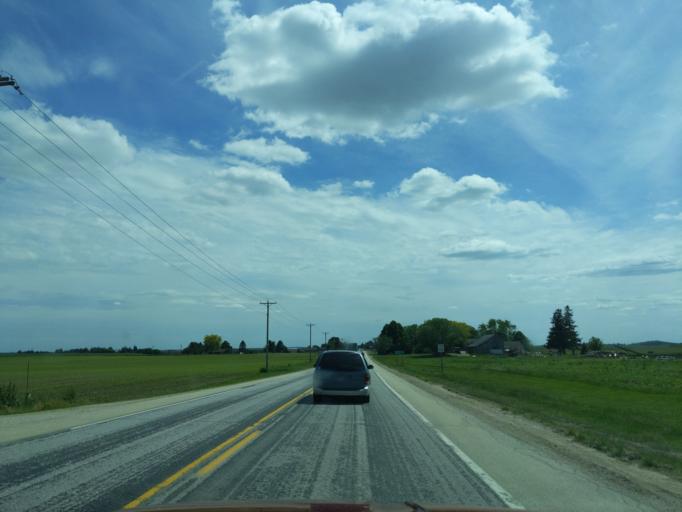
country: US
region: Wisconsin
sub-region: Dane County
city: De Forest
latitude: 43.3285
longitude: -89.3254
